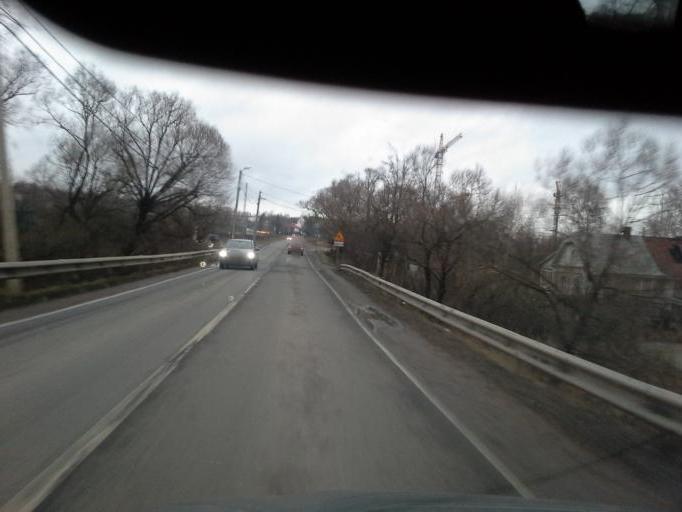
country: RU
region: Moskovskaya
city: Kokoshkino
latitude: 55.6143
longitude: 37.1628
